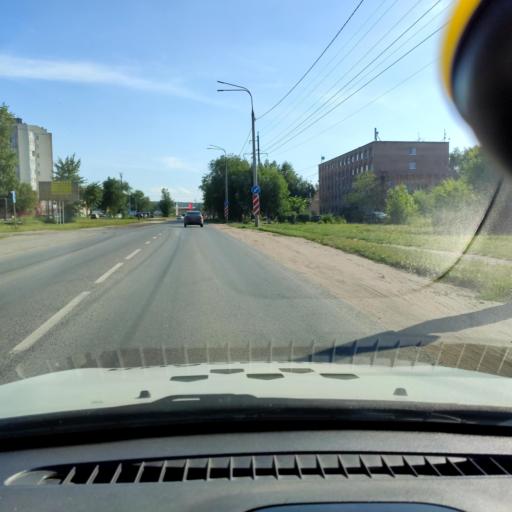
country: RU
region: Samara
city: Zhigulevsk
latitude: 53.4049
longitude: 49.5215
